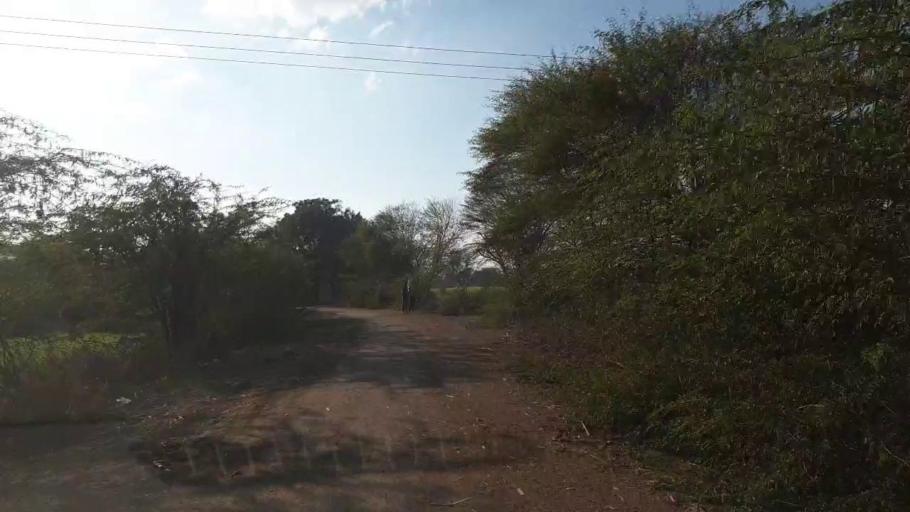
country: PK
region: Sindh
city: Shahpur Chakar
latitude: 26.1241
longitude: 68.5650
